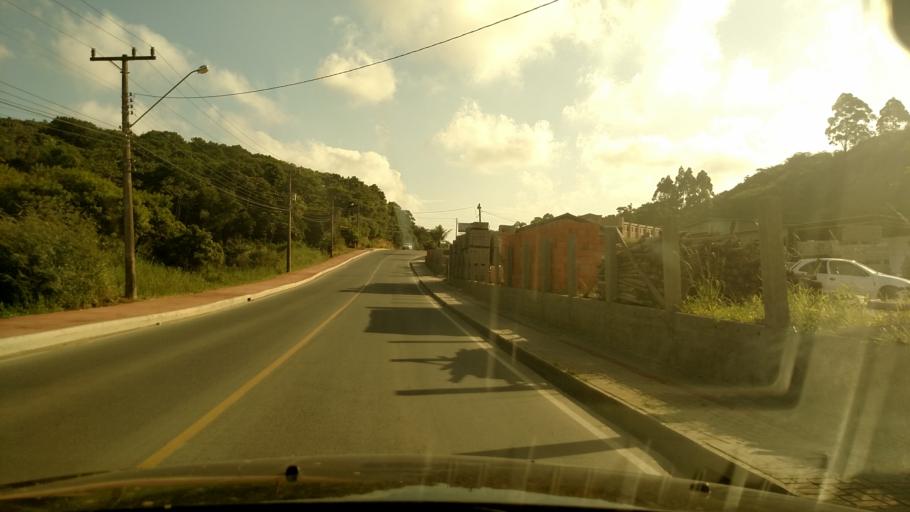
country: BR
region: Santa Catarina
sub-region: Porto Belo
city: Porto Belo
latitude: -27.1584
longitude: -48.5154
